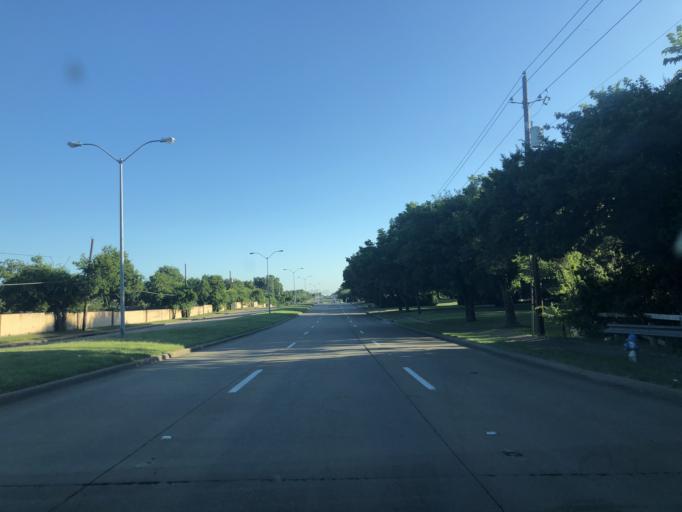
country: US
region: Texas
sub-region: Dallas County
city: Duncanville
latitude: 32.6382
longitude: -96.9427
